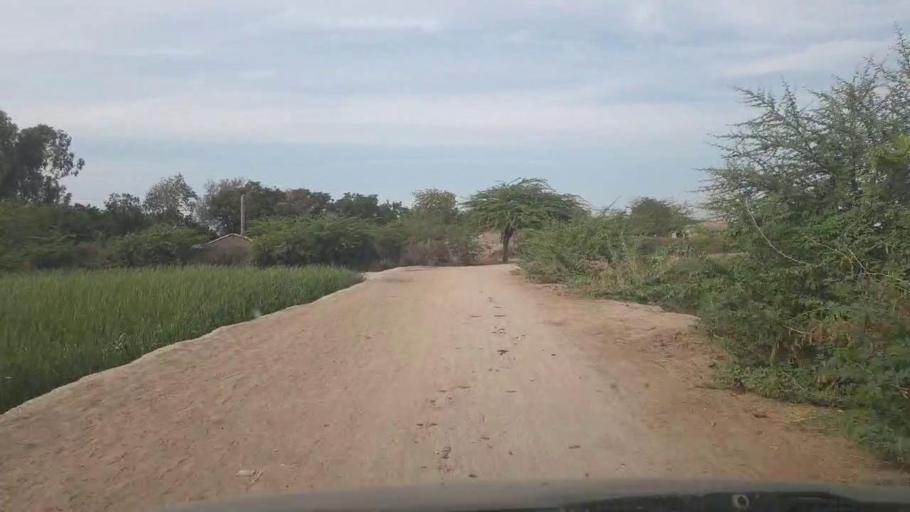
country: PK
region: Sindh
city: Kunri
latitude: 25.2739
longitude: 69.6056
